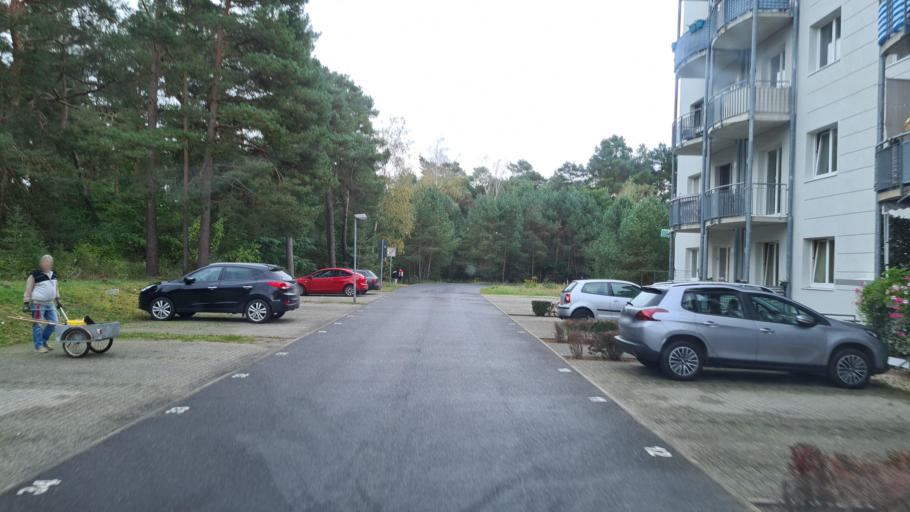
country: DE
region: Brandenburg
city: Zossen
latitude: 52.1765
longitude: 13.4670
